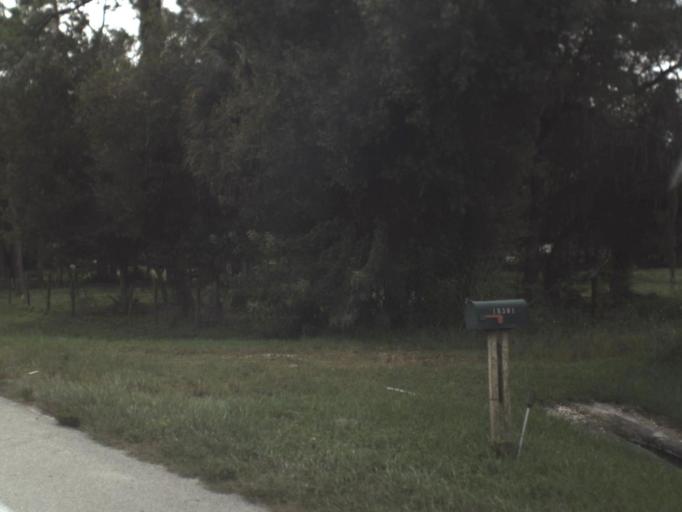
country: US
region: Florida
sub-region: Lee County
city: Fort Myers Shores
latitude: 26.7304
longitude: -81.7610
